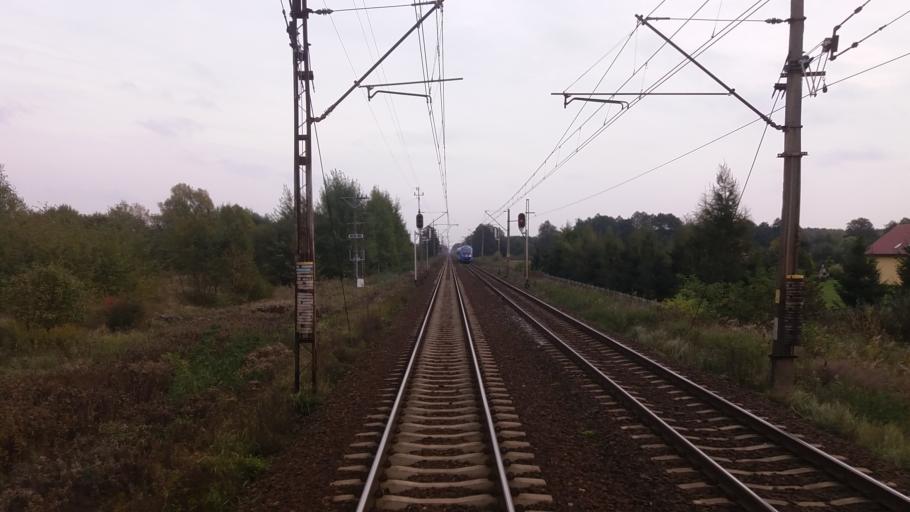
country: PL
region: West Pomeranian Voivodeship
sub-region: Powiat gryfinski
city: Stare Czarnowo
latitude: 53.3860
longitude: 14.7377
